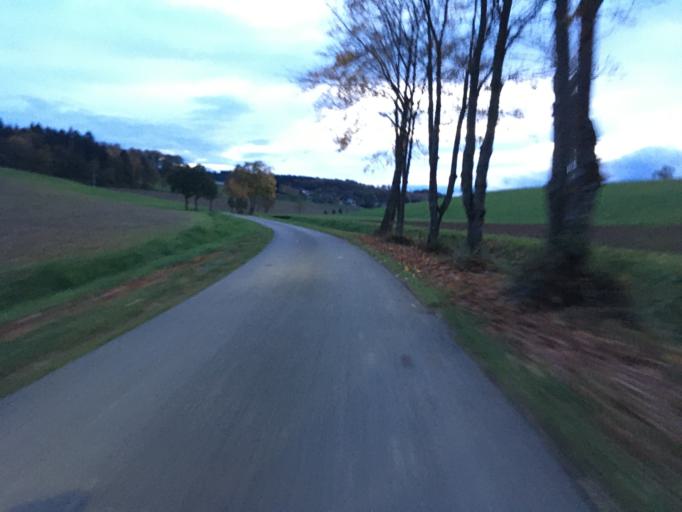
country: DE
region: Baden-Wuerttemberg
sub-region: Karlsruhe Region
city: Adelsheim
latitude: 49.3745
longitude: 9.4311
